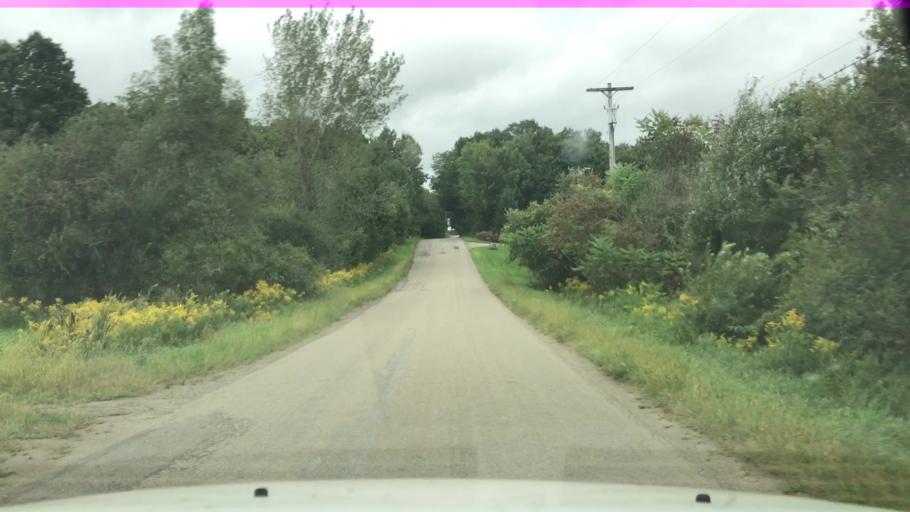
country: US
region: New York
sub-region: Cattaraugus County
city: Little Valley
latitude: 42.3279
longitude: -78.7244
